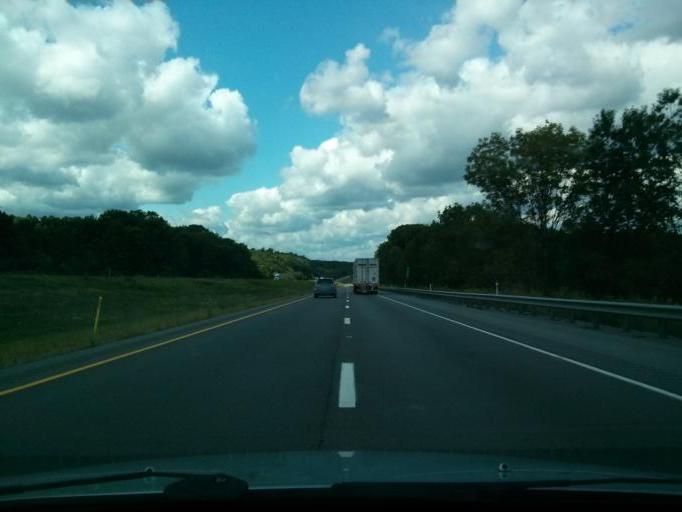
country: US
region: Pennsylvania
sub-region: Clearfield County
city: Treasure Lake
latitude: 41.1218
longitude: -78.6606
